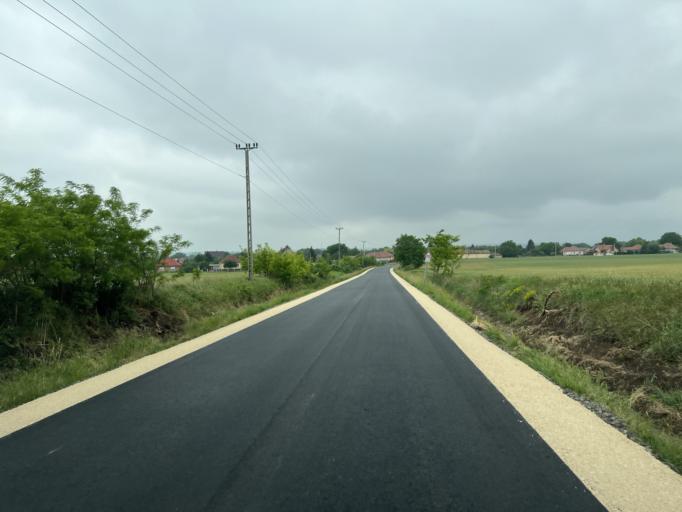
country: HU
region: Pest
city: Vacszentlaszlo
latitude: 47.5776
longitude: 19.5489
